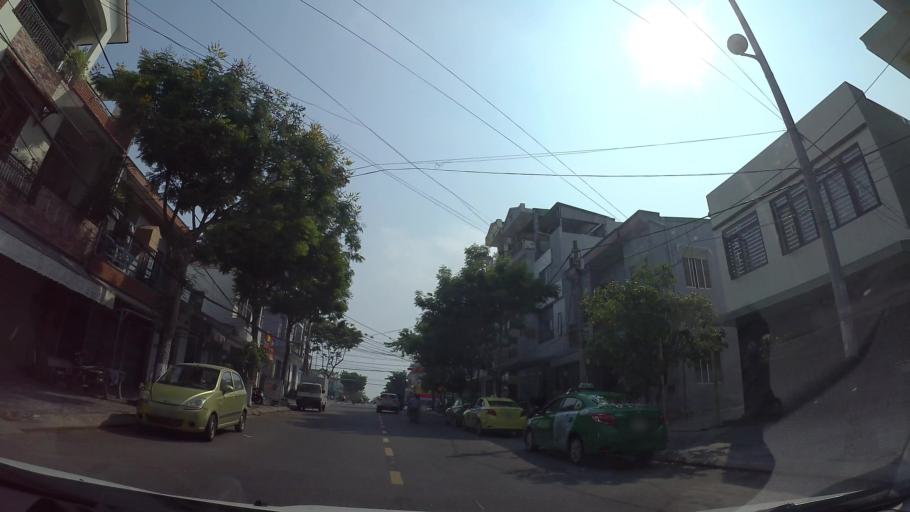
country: VN
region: Da Nang
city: Son Tra
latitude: 16.0417
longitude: 108.2404
